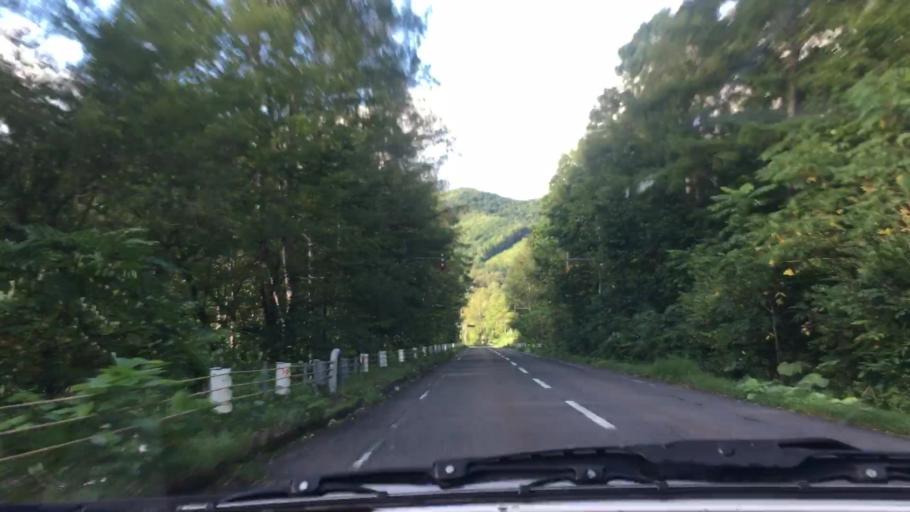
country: JP
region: Hokkaido
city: Otofuke
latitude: 43.1795
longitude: 142.9292
